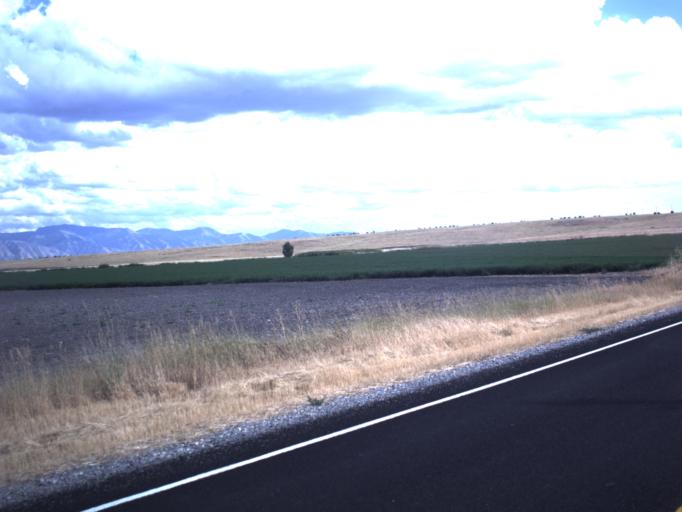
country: US
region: Utah
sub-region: Cache County
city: Benson
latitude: 41.9029
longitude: -112.0457
